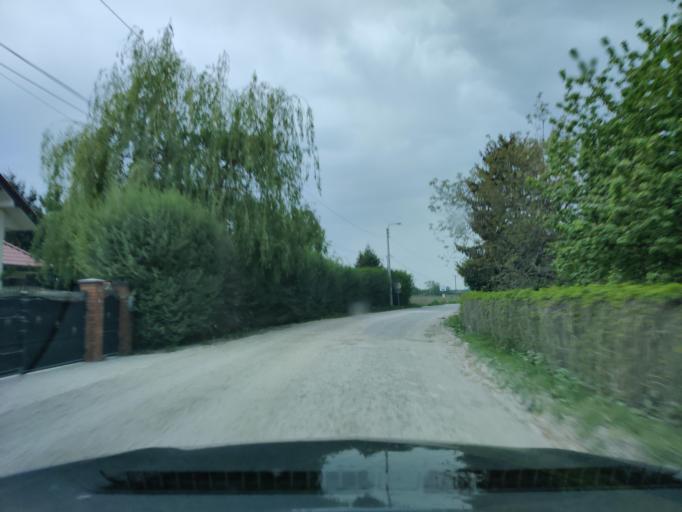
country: PL
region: Masovian Voivodeship
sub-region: Powiat piaseczynski
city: Konstancin-Jeziorna
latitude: 52.1223
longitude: 21.1502
